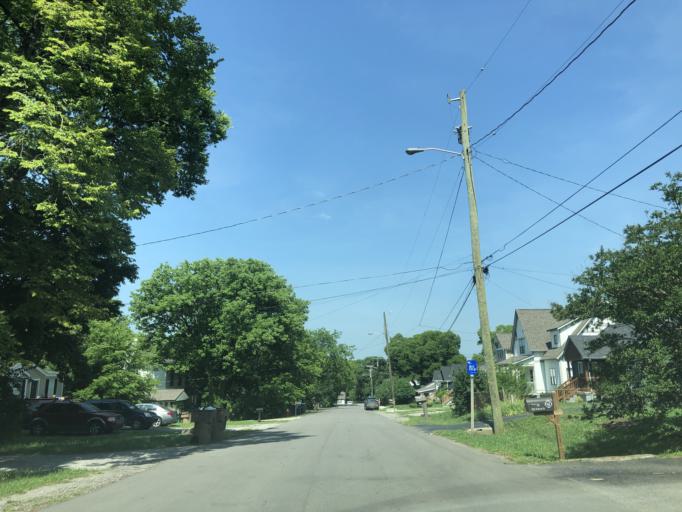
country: US
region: Tennessee
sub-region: Davidson County
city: Nashville
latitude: 36.2045
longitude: -86.7636
